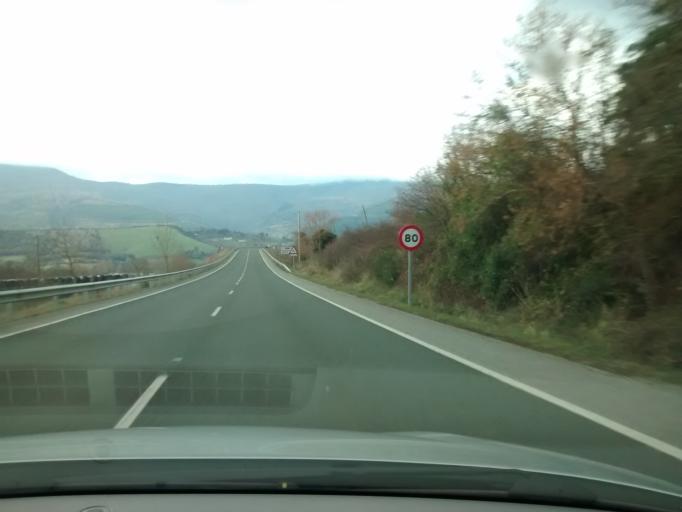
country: ES
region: Castille and Leon
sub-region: Provincia de Burgos
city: Villasana de Mena
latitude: 43.1431
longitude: -3.2651
